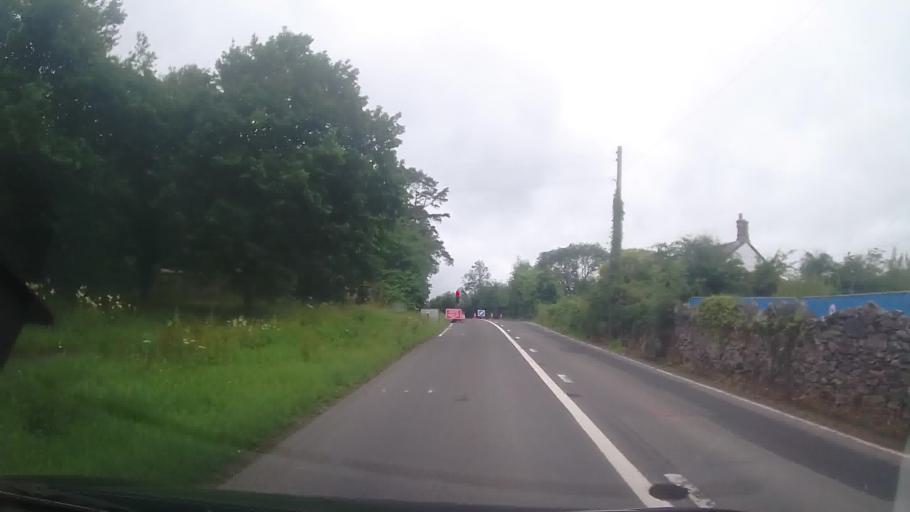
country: GB
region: Wales
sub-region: Anglesey
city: Llanfairpwllgwyngyll
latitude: 53.2176
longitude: -4.2074
